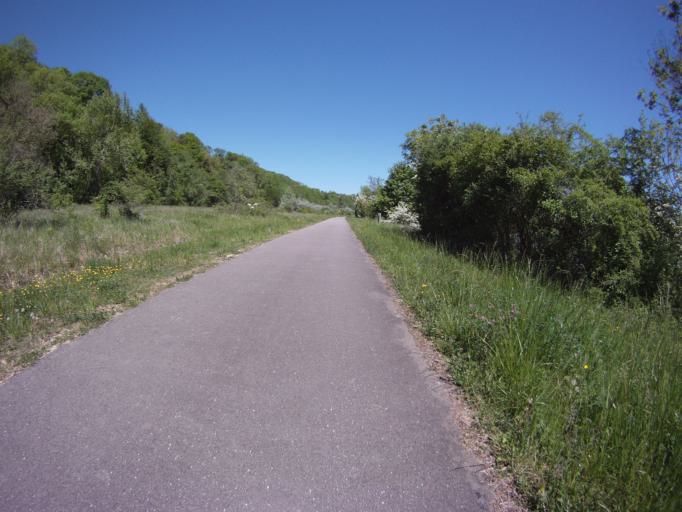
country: FR
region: Lorraine
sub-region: Departement de Meurthe-et-Moselle
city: Villey-Saint-Etienne
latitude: 48.7299
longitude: 5.9812
